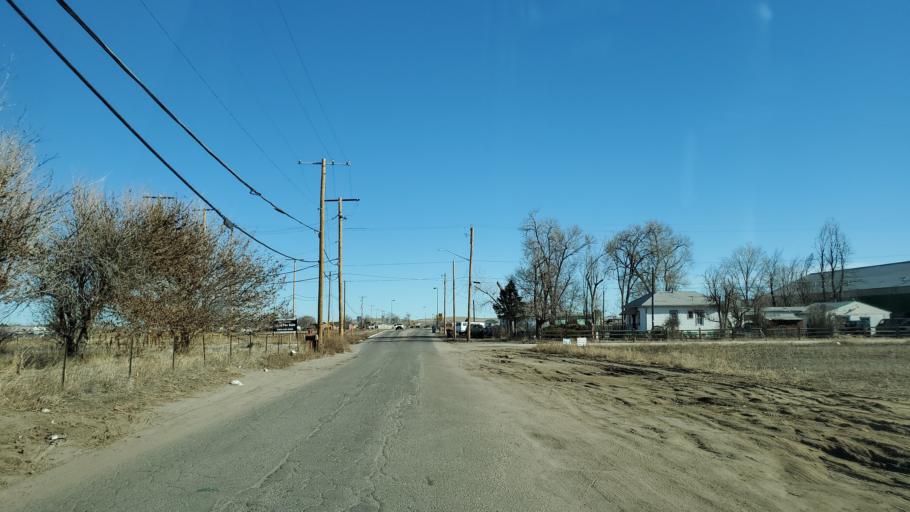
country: US
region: Colorado
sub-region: Adams County
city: Derby
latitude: 39.8490
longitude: -104.8992
